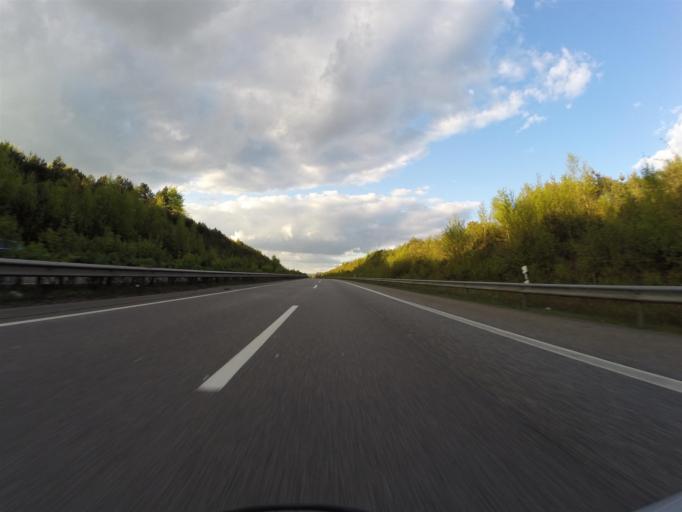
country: DE
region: Rheinland-Pfalz
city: Mehlingen
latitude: 49.4848
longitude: 7.8402
